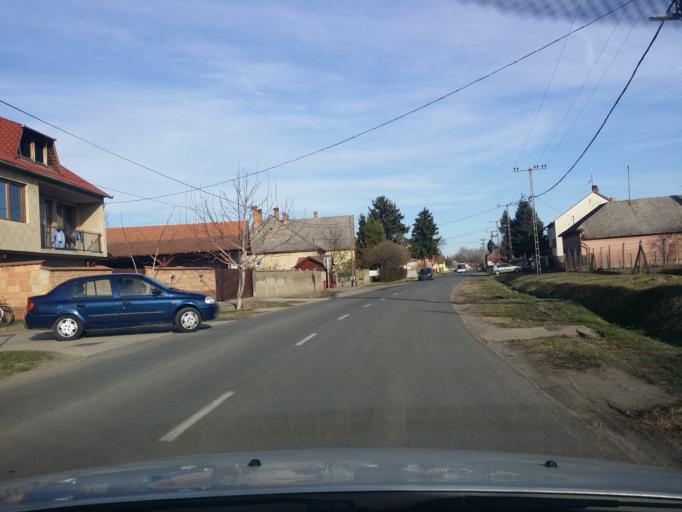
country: HU
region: Tolna
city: Bolcske
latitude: 46.7342
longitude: 18.9609
